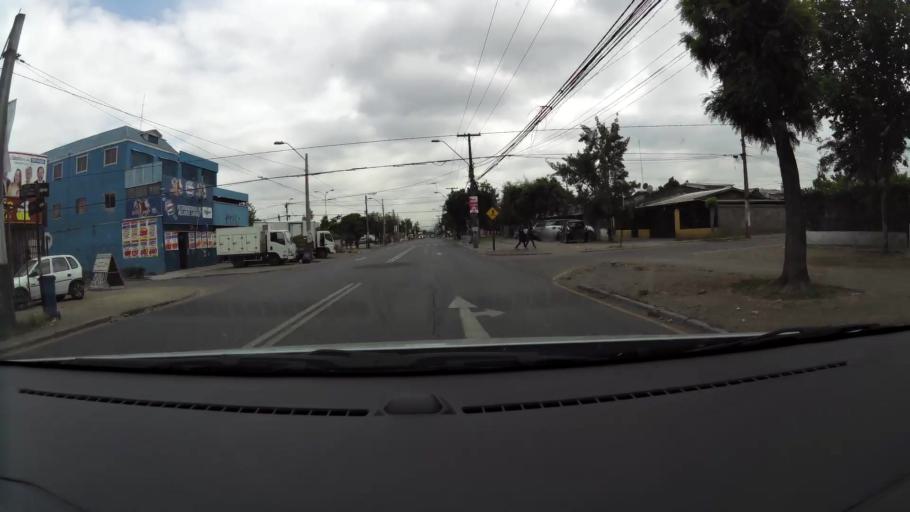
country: CL
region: Santiago Metropolitan
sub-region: Provincia de Santiago
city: Santiago
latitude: -33.5123
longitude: -70.6921
